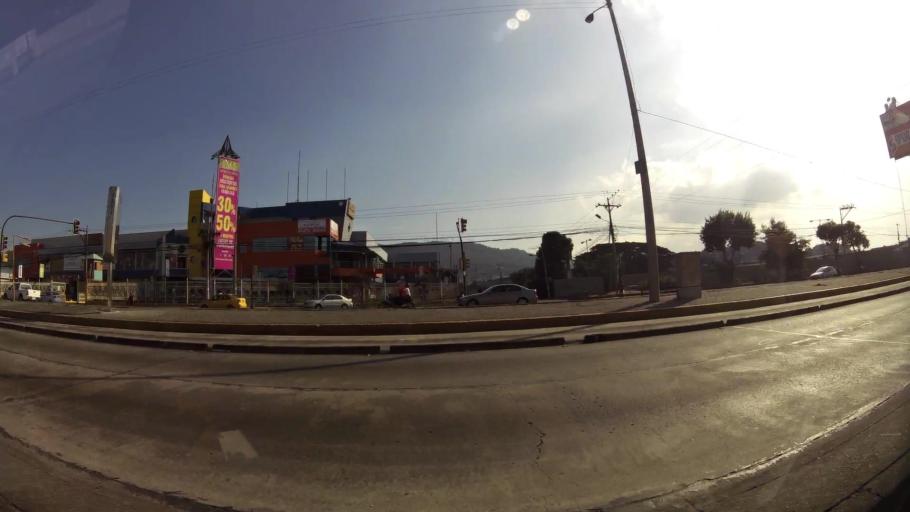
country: EC
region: Guayas
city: Guayaquil
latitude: -2.1549
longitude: -79.9303
